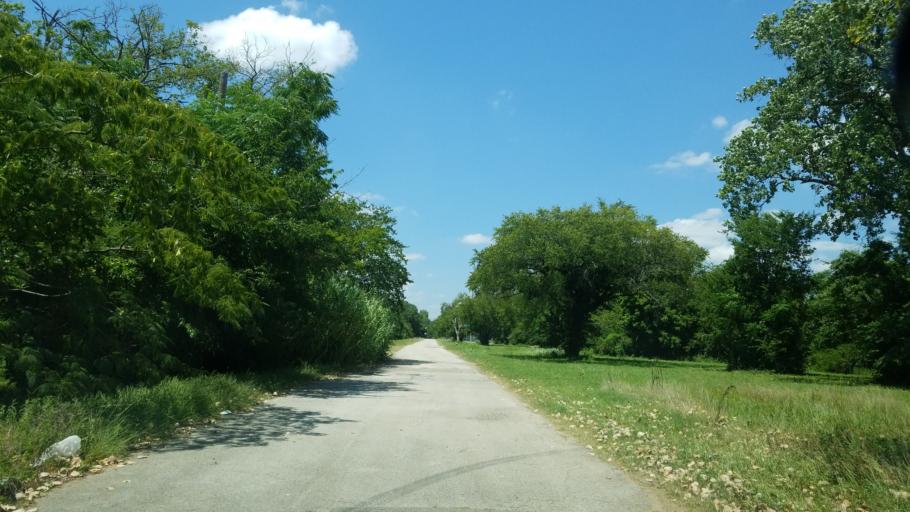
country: US
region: Texas
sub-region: Dallas County
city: Dallas
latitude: 32.7458
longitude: -96.7259
